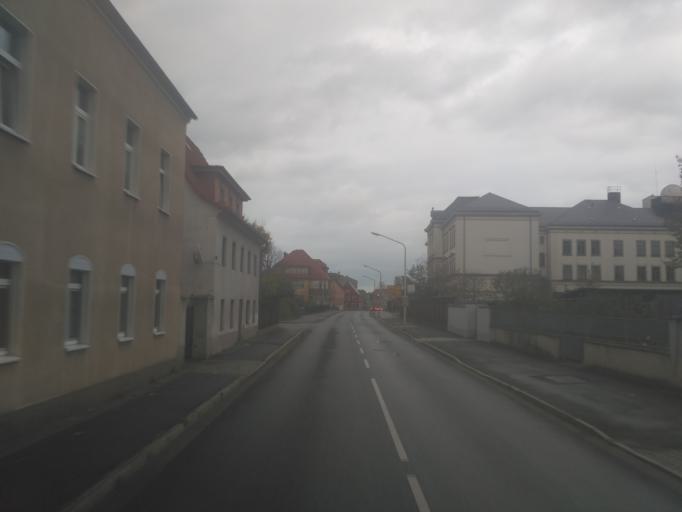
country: DE
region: Saxony
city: Grossenhain
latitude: 51.2946
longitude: 13.5316
